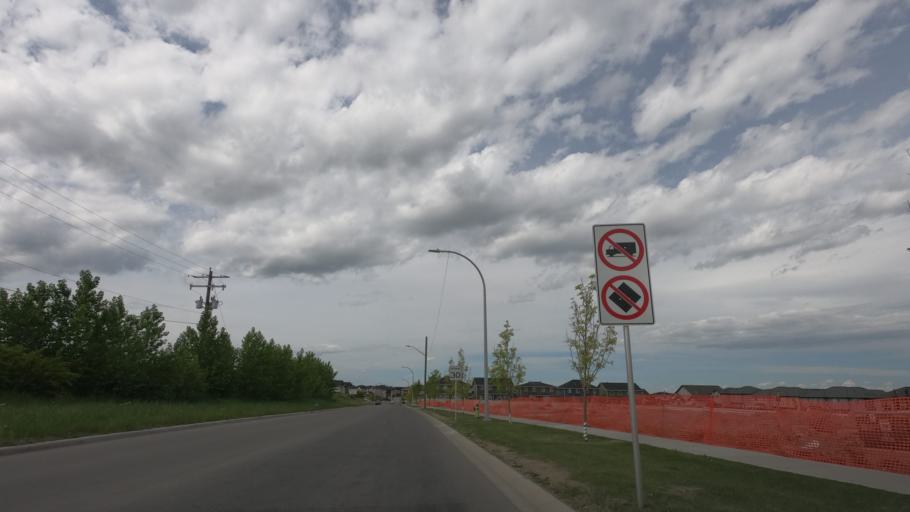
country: CA
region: Alberta
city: Airdrie
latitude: 51.2712
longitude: -114.0424
